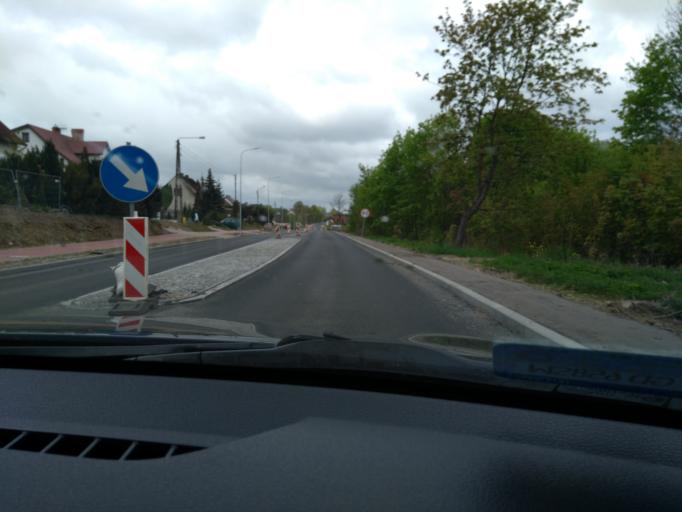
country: PL
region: Pomeranian Voivodeship
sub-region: Powiat kartuski
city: Garcz
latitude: 54.3476
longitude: 18.1180
